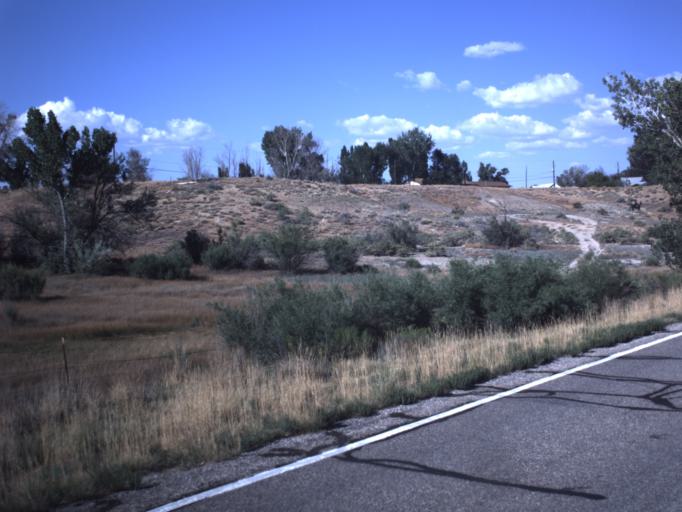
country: US
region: Utah
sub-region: Emery County
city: Huntington
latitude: 39.3478
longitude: -110.8678
